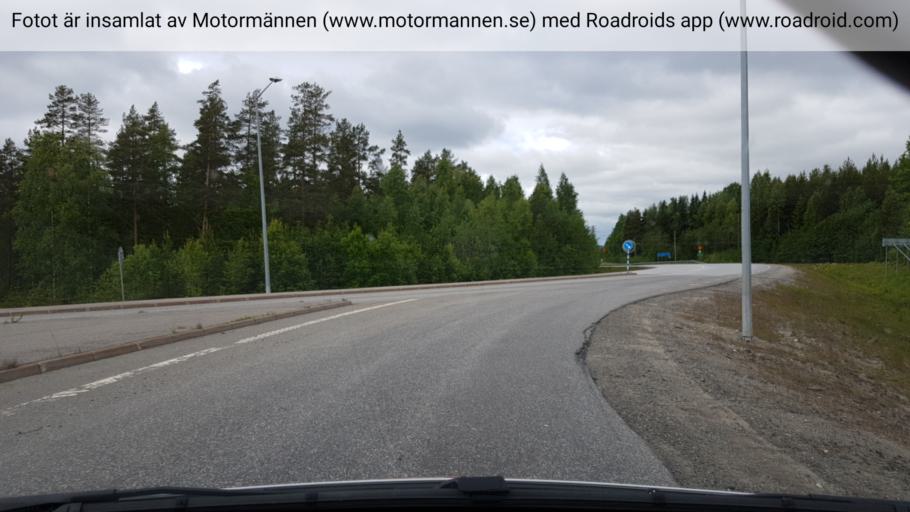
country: SE
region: Vaesterbotten
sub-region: Vannas Kommun
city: Vaennaes
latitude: 63.9224
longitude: 19.7816
